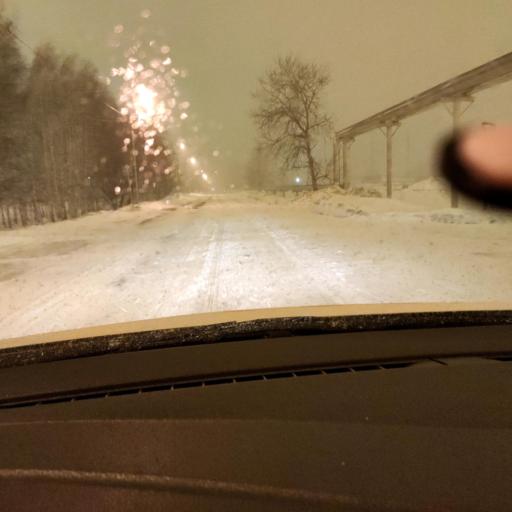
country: RU
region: Tatarstan
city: Osinovo
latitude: 55.8739
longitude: 48.9054
